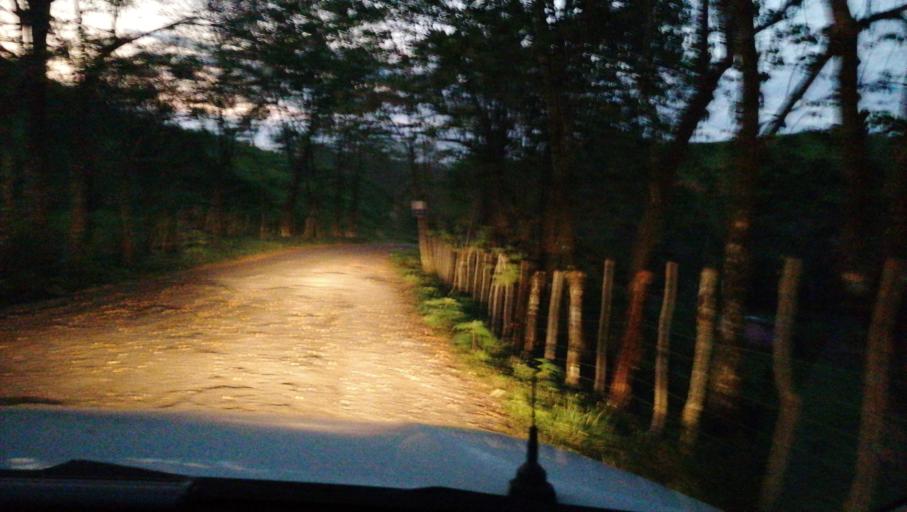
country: MX
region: Chiapas
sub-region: Ostuacan
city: Nuevo Juan del Grijalva
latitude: 17.4807
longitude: -93.3487
